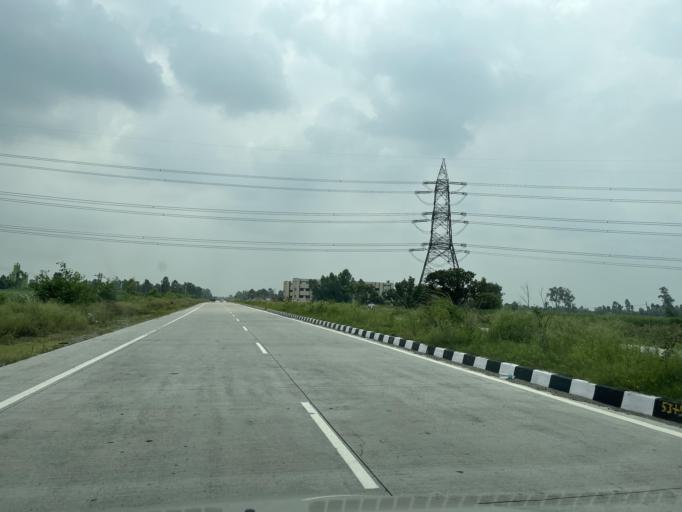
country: IN
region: Uttar Pradesh
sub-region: Bijnor
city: Najibabad
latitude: 29.5640
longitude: 78.3388
